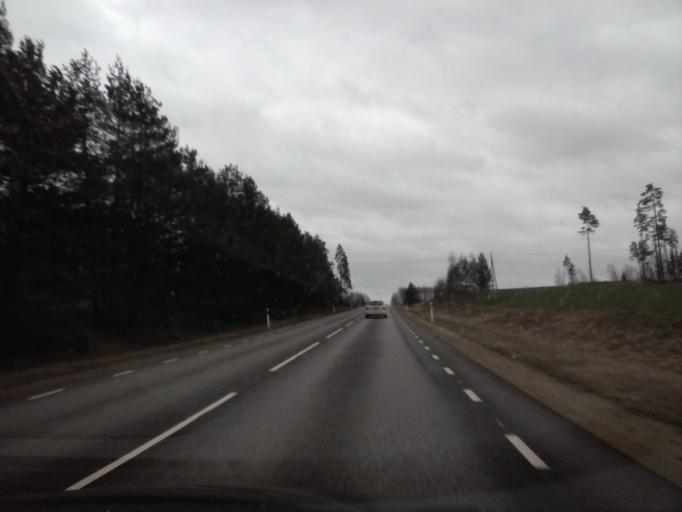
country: EE
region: Polvamaa
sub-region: Polva linn
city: Polva
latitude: 58.0869
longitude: 27.0292
